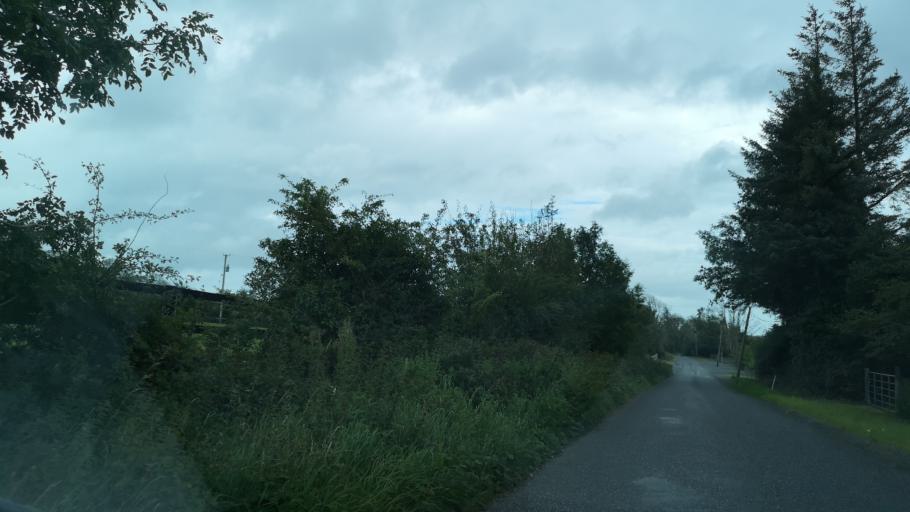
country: IE
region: Connaught
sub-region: County Galway
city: Loughrea
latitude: 53.3060
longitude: -8.6183
